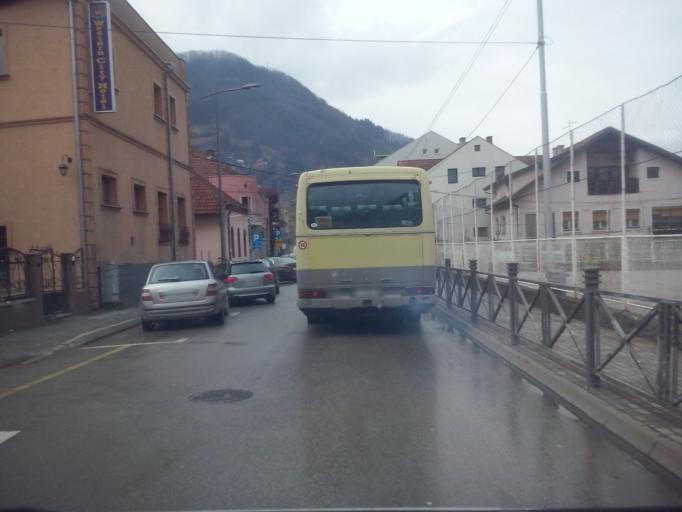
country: RS
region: Central Serbia
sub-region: Moravicki Okrug
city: Ivanjica
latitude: 43.5817
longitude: 20.2285
